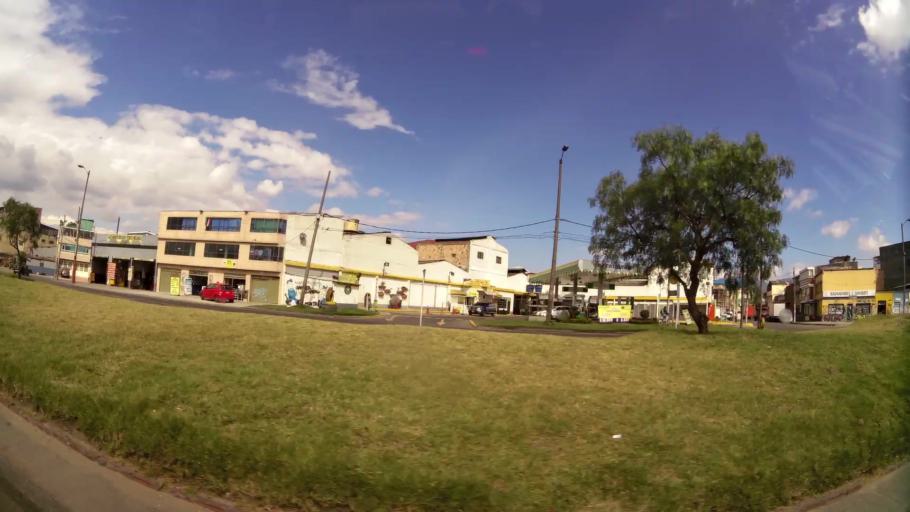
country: CO
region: Bogota D.C.
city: Bogota
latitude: 4.6154
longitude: -74.1405
